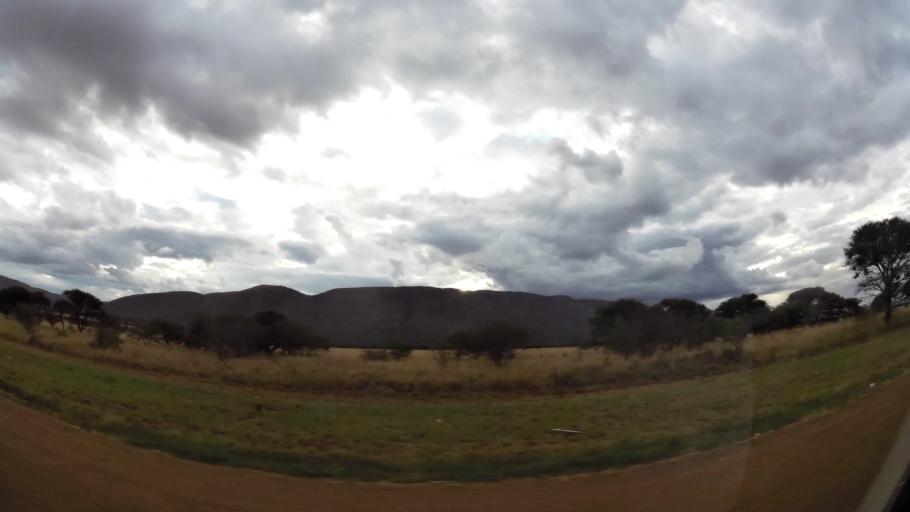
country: ZA
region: Limpopo
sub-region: Waterberg District Municipality
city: Mokopane
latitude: -24.2528
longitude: 28.9894
